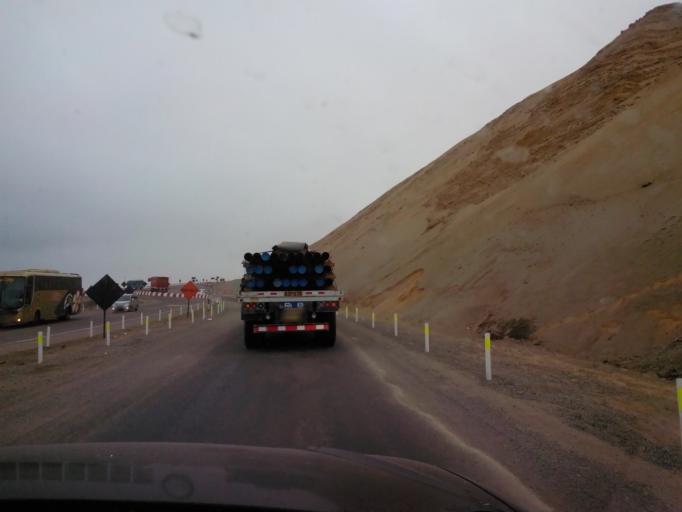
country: PE
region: Ica
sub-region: Provincia de Chincha
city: San Pedro
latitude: -13.3226
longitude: -76.2433
